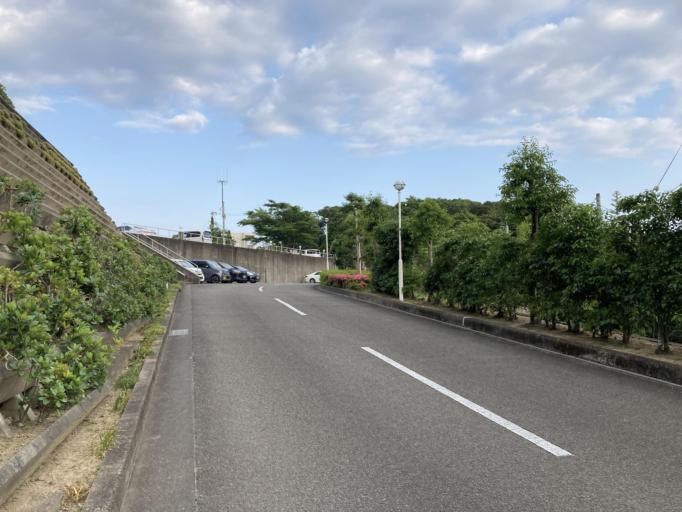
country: JP
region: Wakayama
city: Tanabe
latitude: 33.6824
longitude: 135.3575
